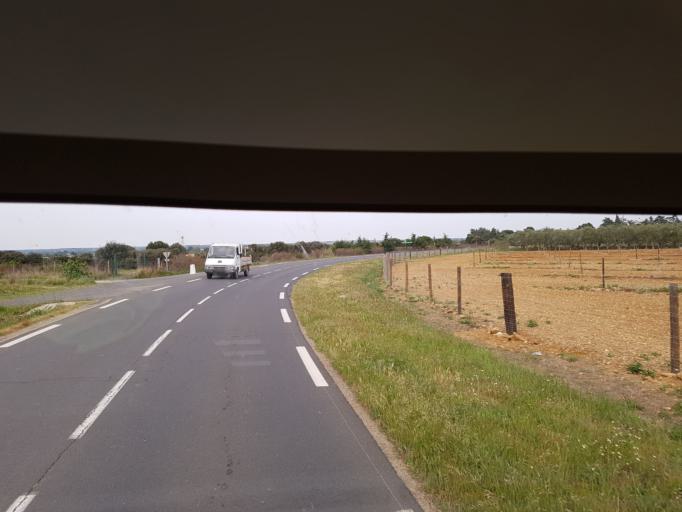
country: FR
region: Languedoc-Roussillon
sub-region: Departement de l'Herault
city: Serignan
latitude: 43.2746
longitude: 3.2641
